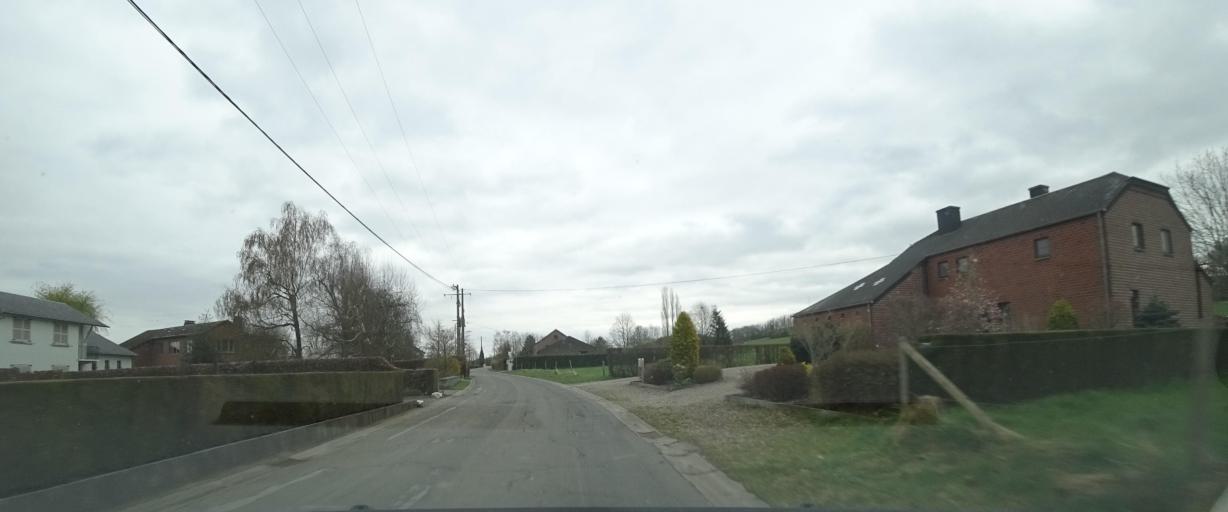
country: BE
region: Wallonia
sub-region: Province du Luxembourg
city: Marche-en-Famenne
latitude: 50.2208
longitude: 5.3522
